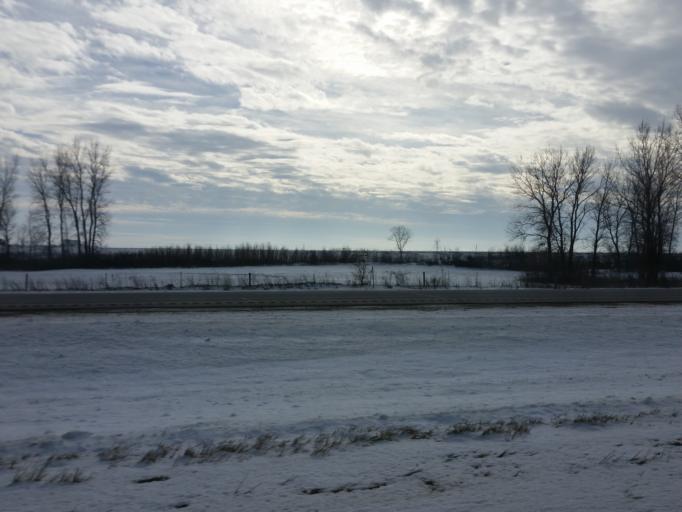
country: US
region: Iowa
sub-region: Buchanan County
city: Independence
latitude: 42.4484
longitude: -91.9149
